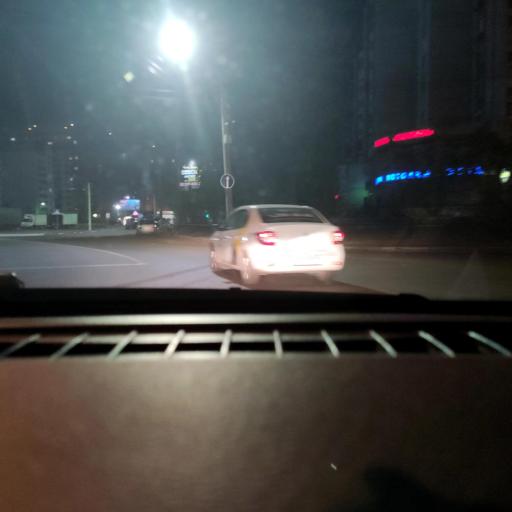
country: RU
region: Voronezj
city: Podgornoye
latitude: 51.7124
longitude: 39.1627
